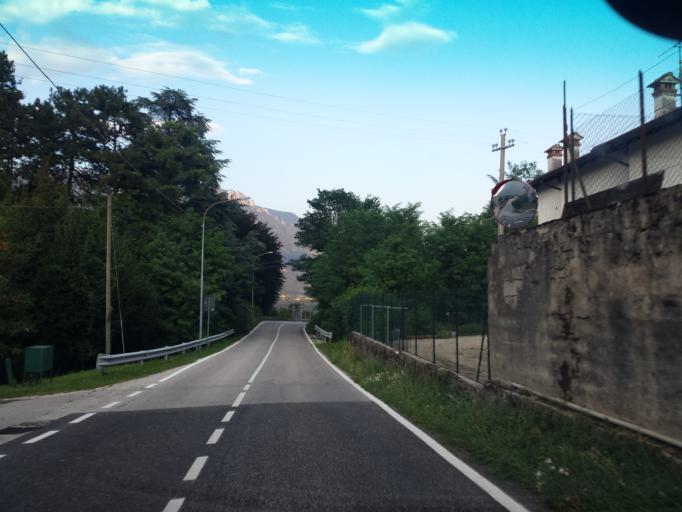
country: IT
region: Veneto
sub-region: Provincia di Vicenza
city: Velo d'Astico
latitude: 45.7870
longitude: 11.3722
